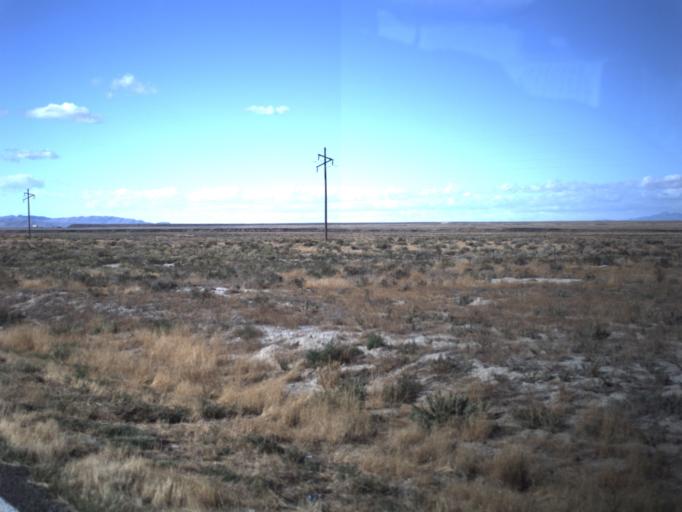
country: US
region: Utah
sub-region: Millard County
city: Delta
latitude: 39.2140
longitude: -112.6794
